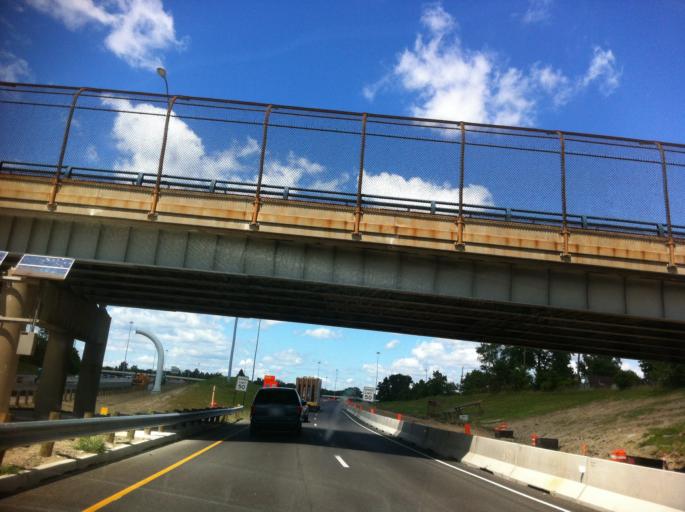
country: US
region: Ohio
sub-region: Lucas County
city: Toledo
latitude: 41.6703
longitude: -83.5726
